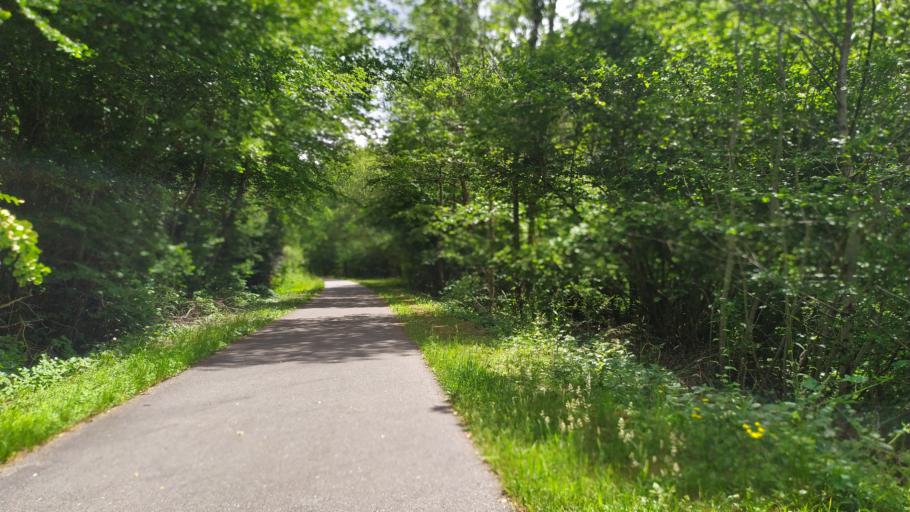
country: BE
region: Wallonia
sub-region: Province de Namur
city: Rochefort
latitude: 50.1546
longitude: 5.2402
